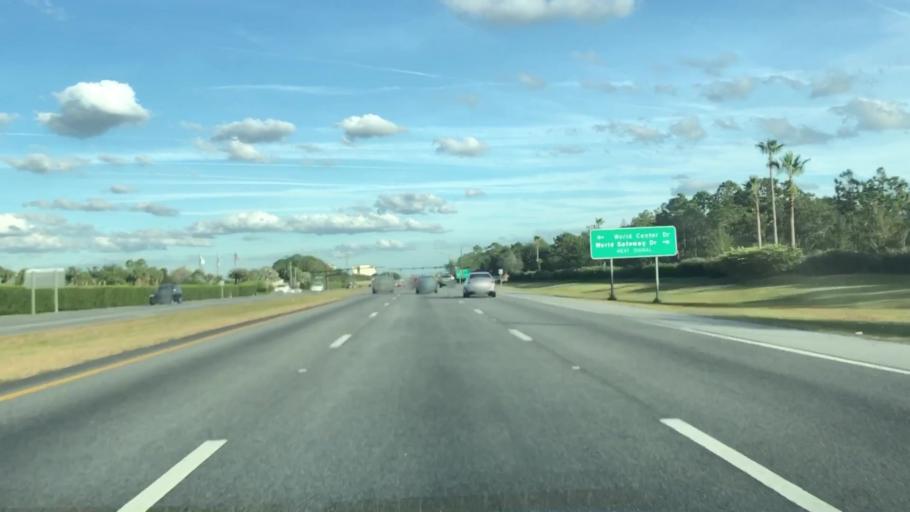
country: US
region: Florida
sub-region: Osceola County
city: Celebration
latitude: 28.3579
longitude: -81.5085
